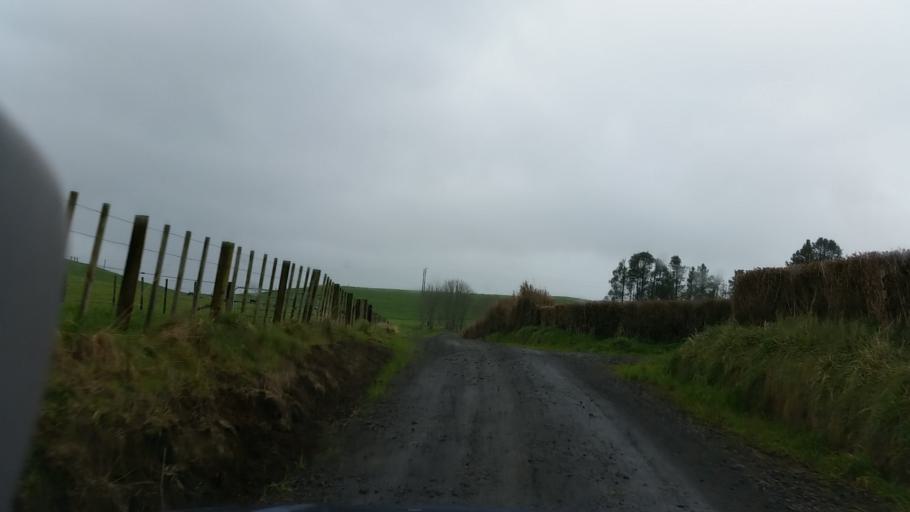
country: NZ
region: Taranaki
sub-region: South Taranaki District
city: Eltham
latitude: -39.2817
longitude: 174.3353
